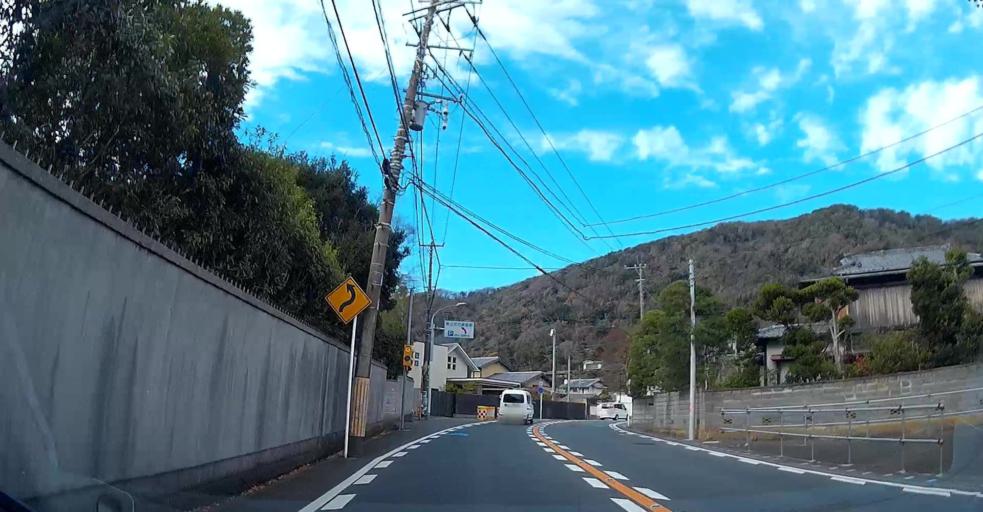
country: JP
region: Kanagawa
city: Hayama
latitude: 35.2645
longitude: 139.5781
